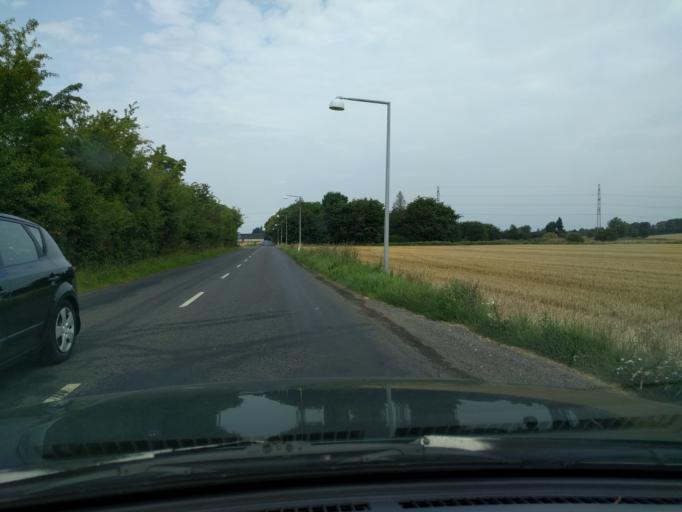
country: DK
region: South Denmark
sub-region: Odense Kommune
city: Neder Holluf
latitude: 55.3907
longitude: 10.4657
